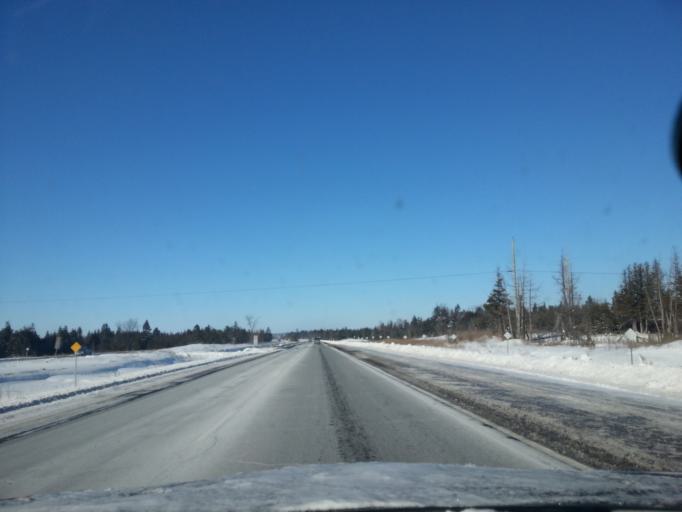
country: CA
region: Ontario
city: Arnprior
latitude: 45.3464
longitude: -76.2005
